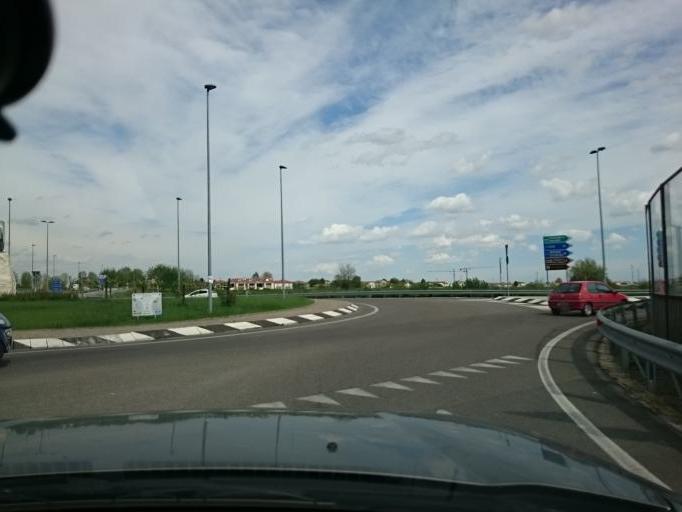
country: IT
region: Veneto
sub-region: Provincia di Vicenza
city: Longare
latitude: 45.4795
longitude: 11.6099
